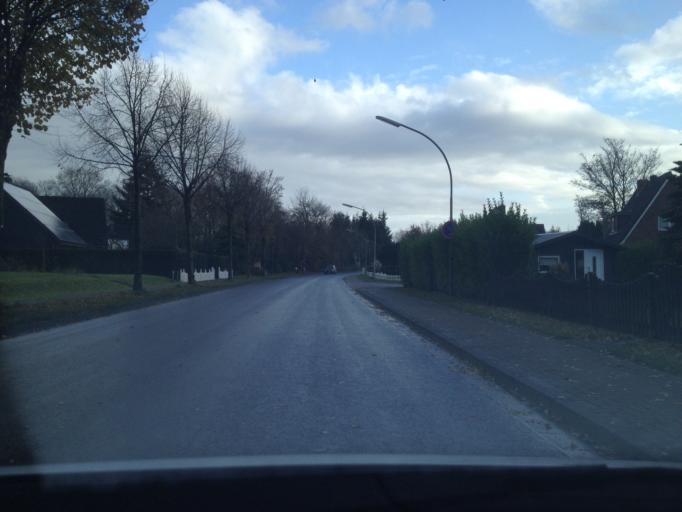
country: DE
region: Schleswig-Holstein
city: Leck
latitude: 54.7777
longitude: 8.9647
